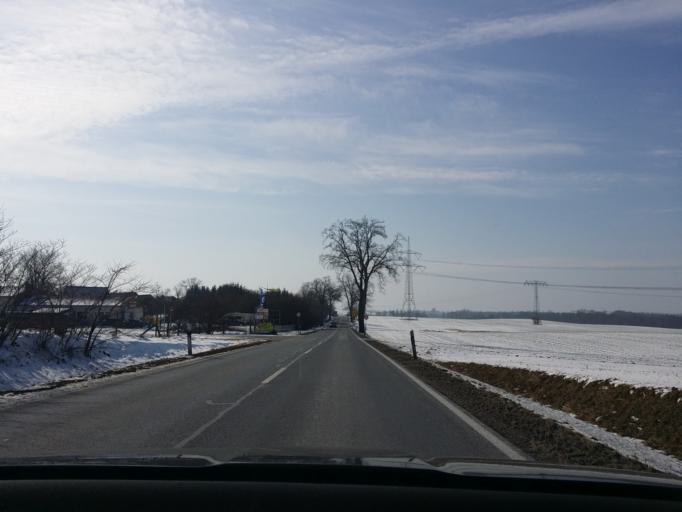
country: DE
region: Mecklenburg-Vorpommern
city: Penzlin
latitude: 53.5217
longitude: 13.1264
